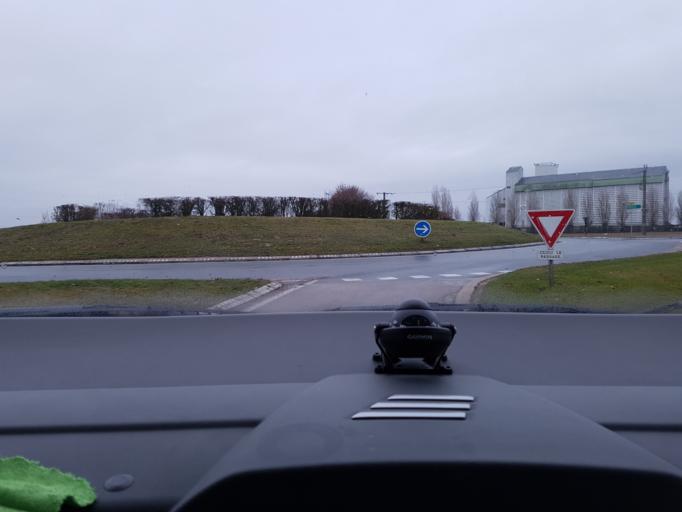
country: FR
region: Haute-Normandie
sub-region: Departement de l'Eure
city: Le Neubourg
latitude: 49.1196
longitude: 0.8609
